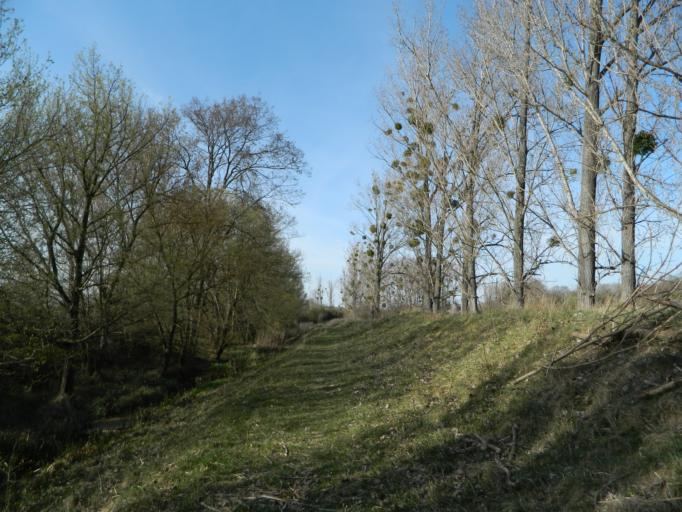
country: HU
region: Fejer
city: Pakozd
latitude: 47.2251
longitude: 18.4885
